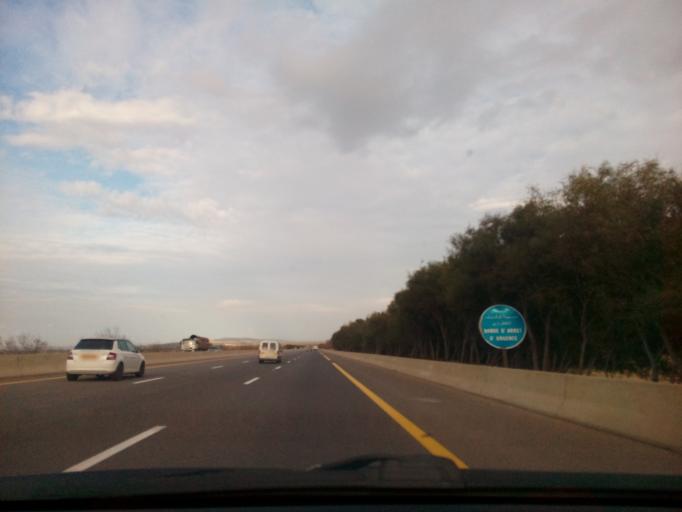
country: DZ
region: Mostaganem
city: Mostaganem
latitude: 35.6758
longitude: 0.1495
